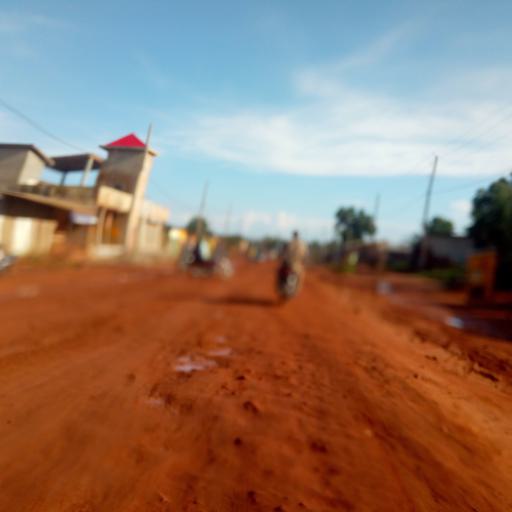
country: BJ
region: Atlantique
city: Hevie
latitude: 6.4209
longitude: 2.2608
